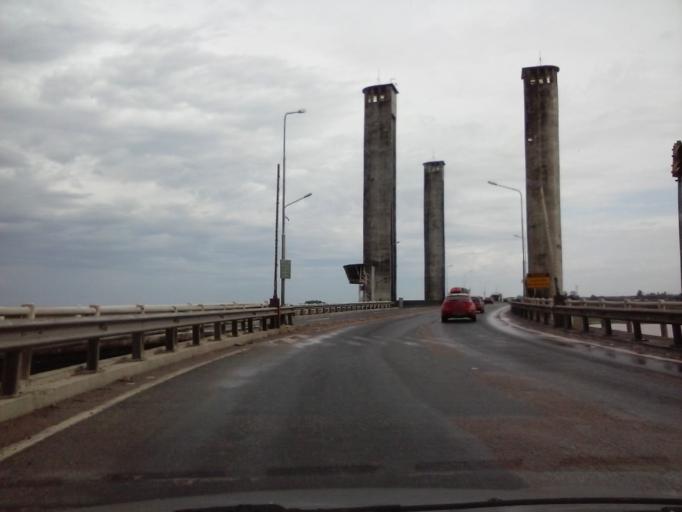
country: BR
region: Rio Grande do Sul
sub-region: Porto Alegre
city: Porto Alegre
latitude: -29.9977
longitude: -51.2074
